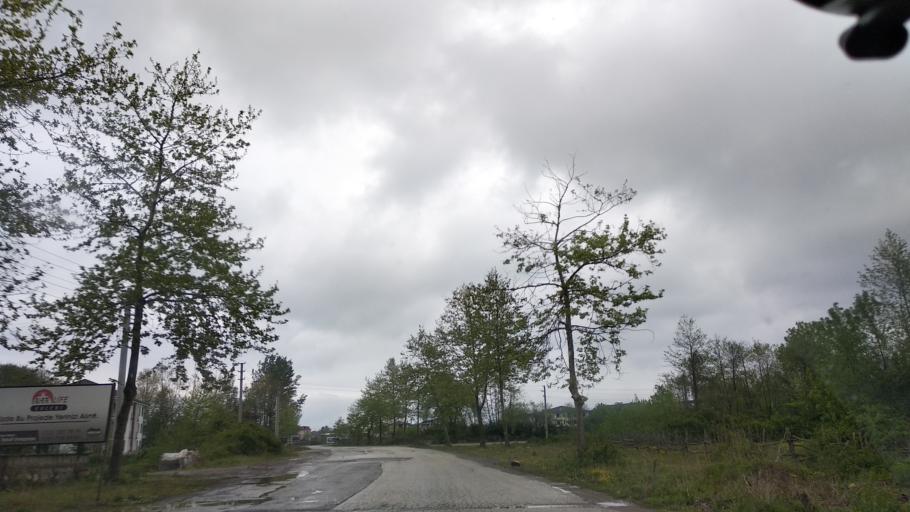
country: TR
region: Sakarya
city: Karasu
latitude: 41.0928
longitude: 30.7077
